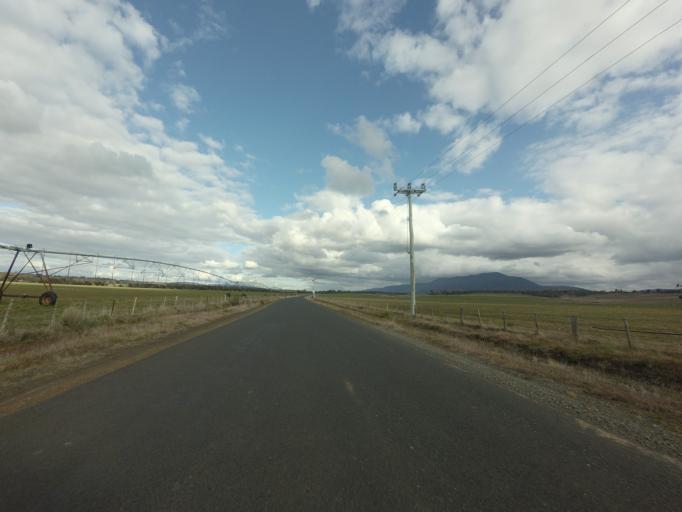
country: AU
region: Tasmania
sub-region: Northern Midlands
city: Longford
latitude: -41.8213
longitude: 147.2026
